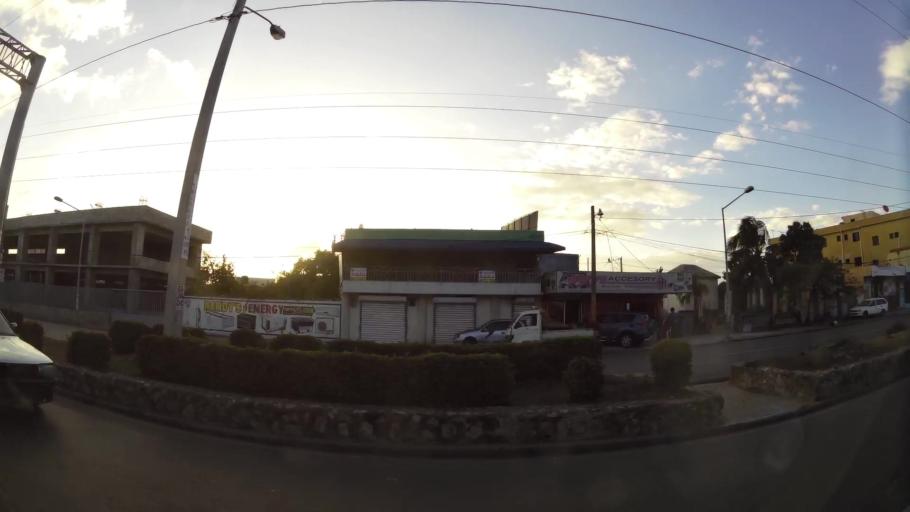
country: DO
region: Santo Domingo
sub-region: Santo Domingo
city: Santo Domingo Este
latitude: 18.4858
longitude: -69.8266
